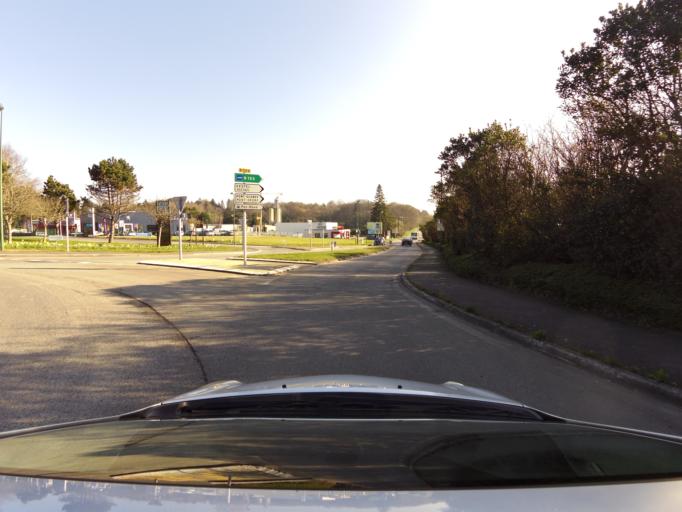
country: FR
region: Brittany
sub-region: Departement du Morbihan
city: Gestel
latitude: 47.8019
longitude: -3.4783
